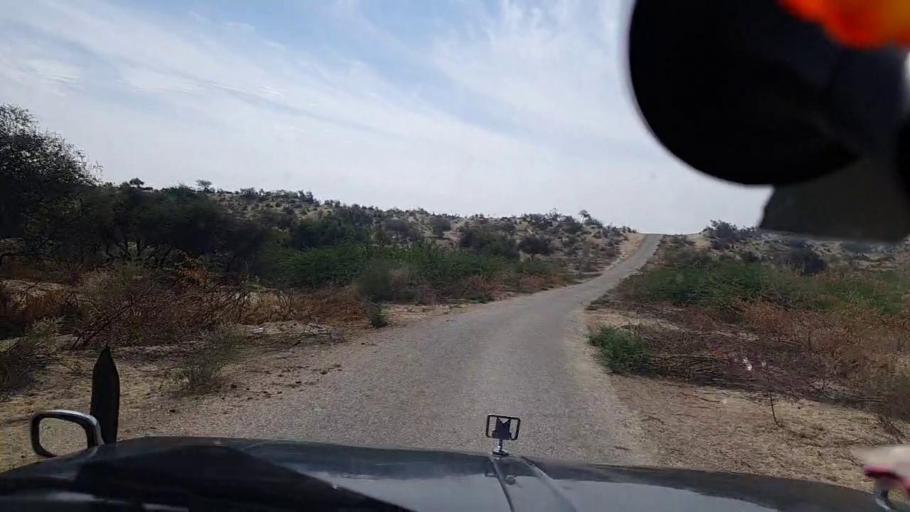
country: PK
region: Sindh
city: Diplo
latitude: 24.4042
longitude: 69.5878
